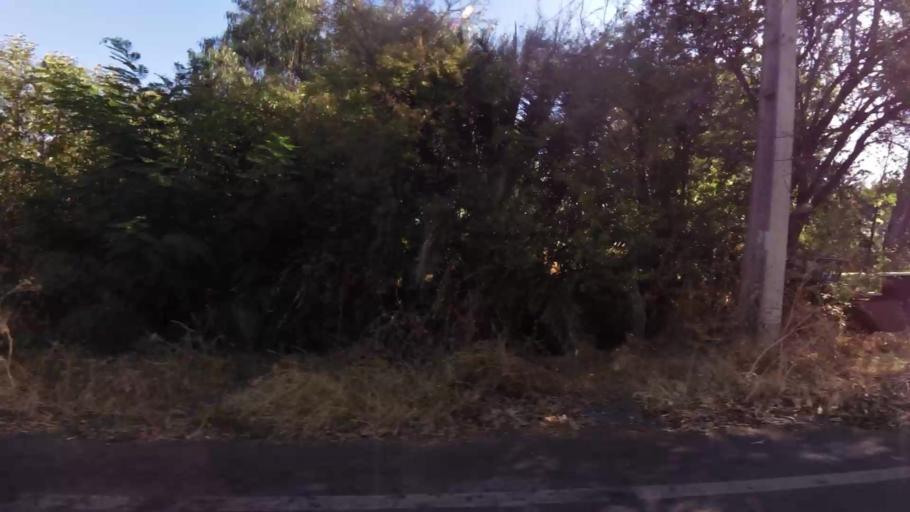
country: CL
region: Maule
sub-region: Provincia de Talca
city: Talca
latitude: -35.4052
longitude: -71.6037
